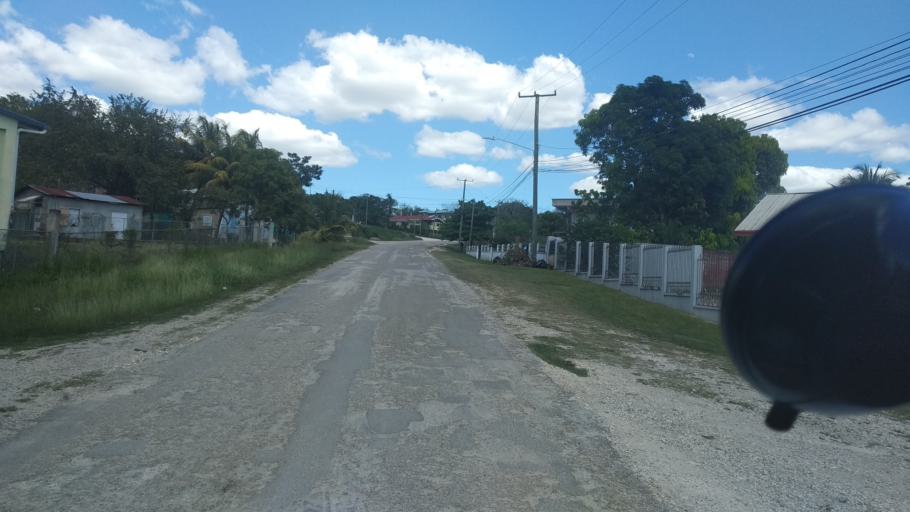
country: BZ
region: Cayo
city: Benque Viejo del Carmen
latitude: 17.0757
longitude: -89.1322
